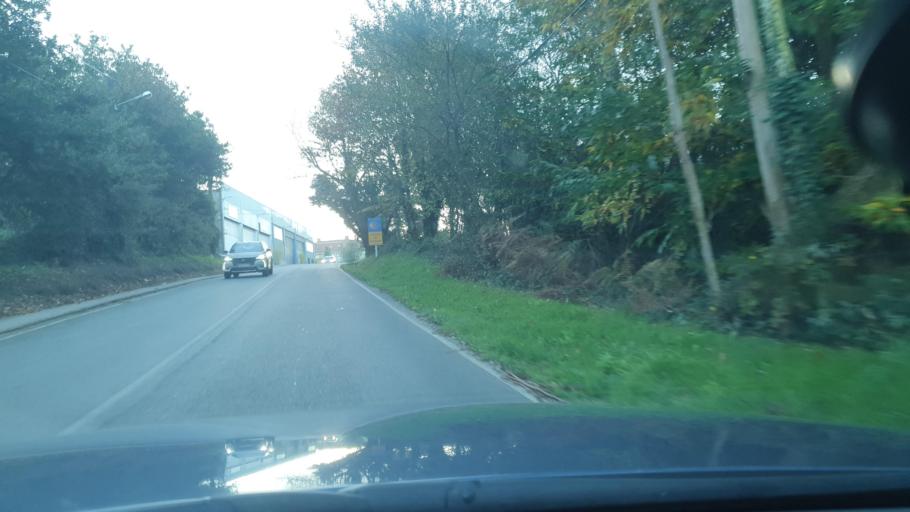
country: ES
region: Galicia
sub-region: Provincia da Coruna
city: Santiago de Compostela
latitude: 42.8439
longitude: -8.5836
